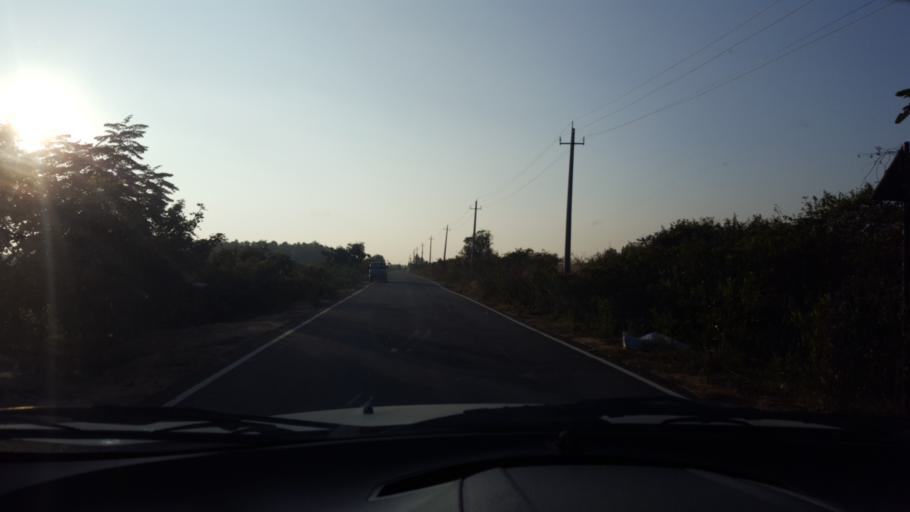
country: IN
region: Karnataka
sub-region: Bangalore Urban
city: Yelahanka
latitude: 13.1897
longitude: 77.6041
